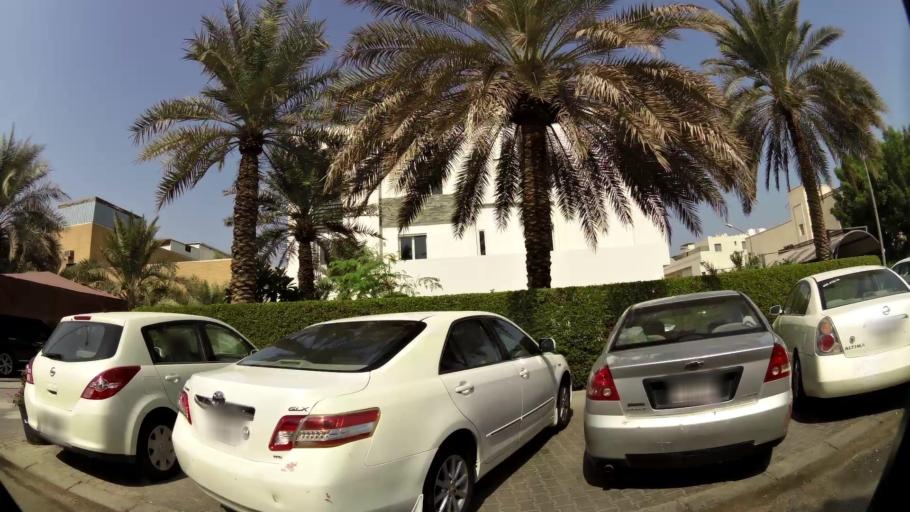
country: KW
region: Al Asimah
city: Ad Dasmah
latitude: 29.3581
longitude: 48.0171
